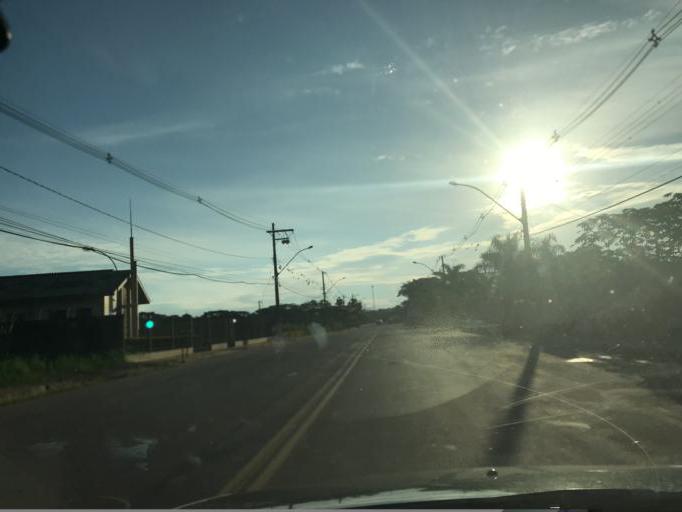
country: BR
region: Minas Gerais
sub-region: Tres Coracoes
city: Tres Coracoes
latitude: -21.7020
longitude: -45.2424
